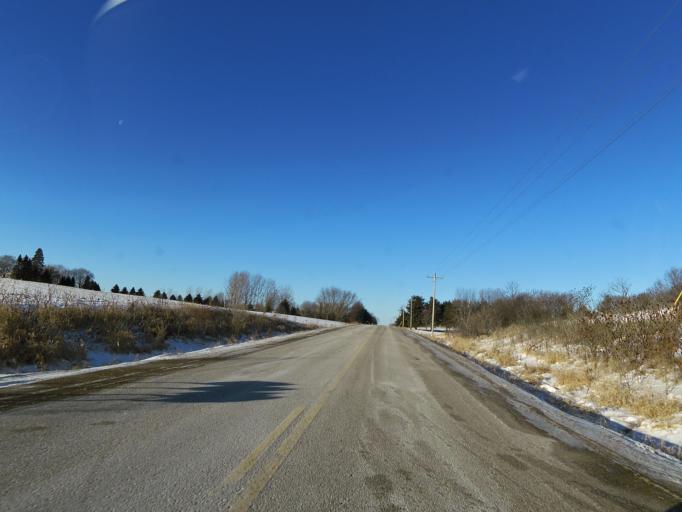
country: US
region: Minnesota
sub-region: Scott County
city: Jordan
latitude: 44.6599
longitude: -93.5935
